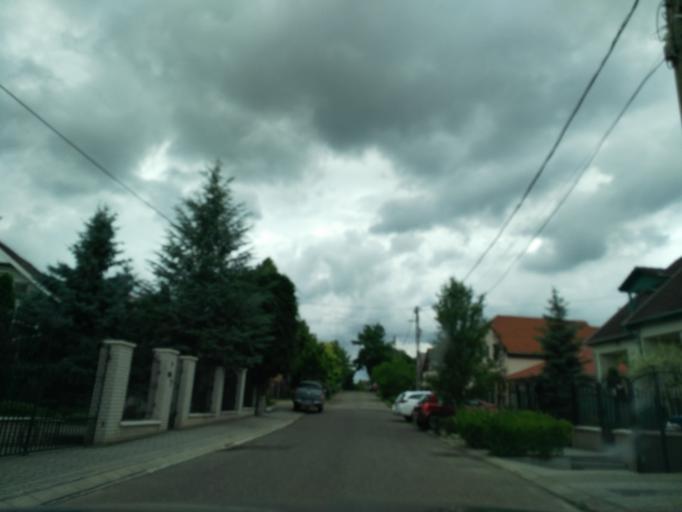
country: HU
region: Hajdu-Bihar
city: Debrecen
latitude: 47.5431
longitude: 21.6569
